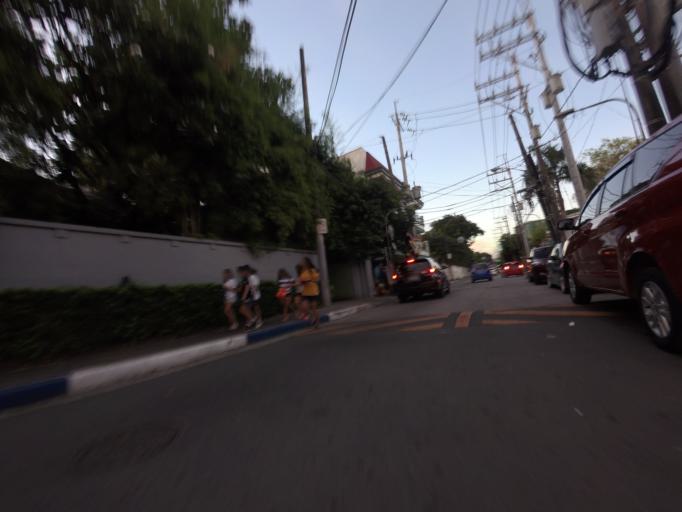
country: PH
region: Metro Manila
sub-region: City of Manila
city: Quiapo
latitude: 14.5932
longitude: 120.9932
